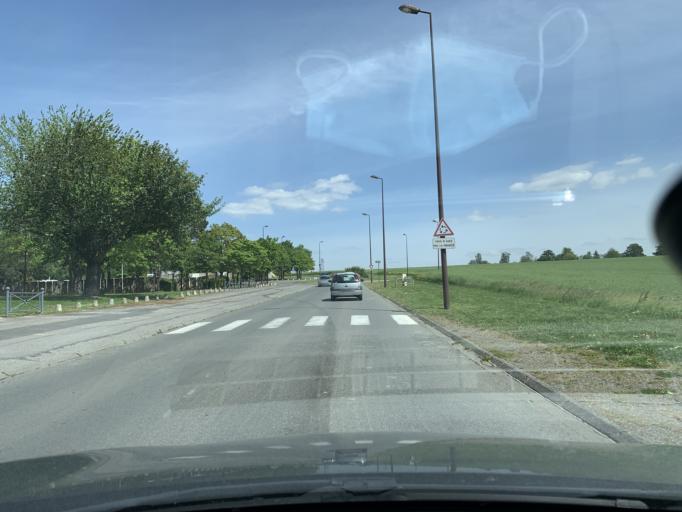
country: FR
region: Picardie
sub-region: Departement de l'Aisne
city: Saint-Quentin
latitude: 49.8648
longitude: 3.2796
